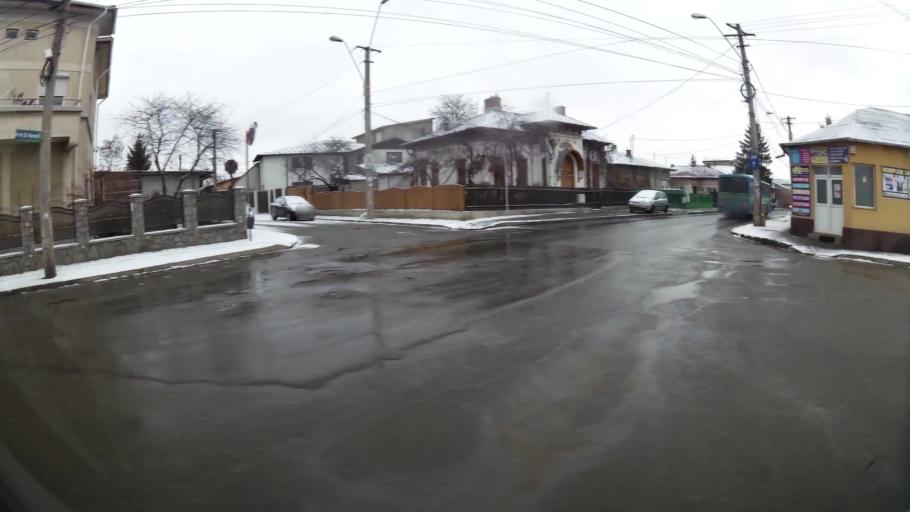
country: RO
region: Prahova
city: Ploiesti
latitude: 44.9340
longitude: 26.0350
